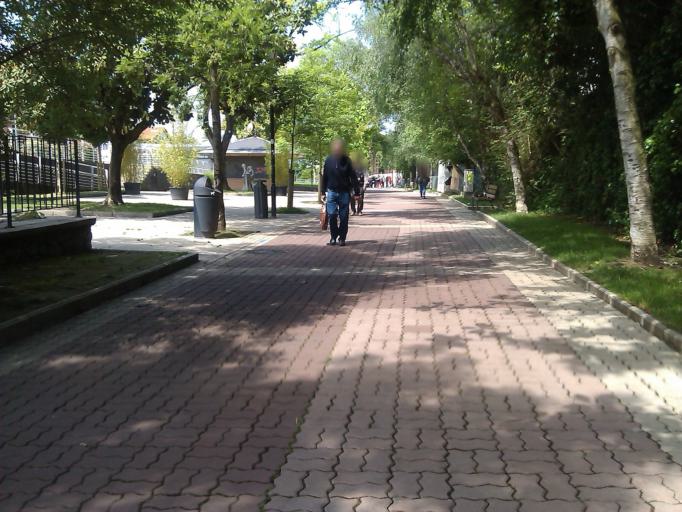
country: ES
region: Basque Country
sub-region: Provincia de Guipuzcoa
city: Pasaia
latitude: 43.3200
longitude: -1.9507
